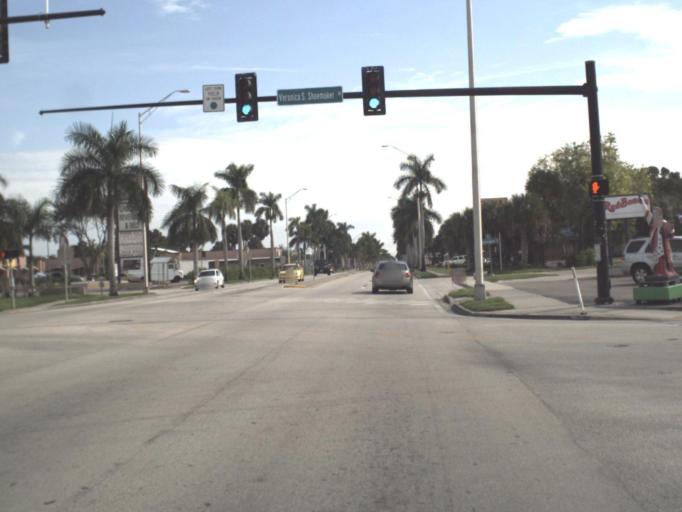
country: US
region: Florida
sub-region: Lee County
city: Tice
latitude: 26.6605
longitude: -81.8408
